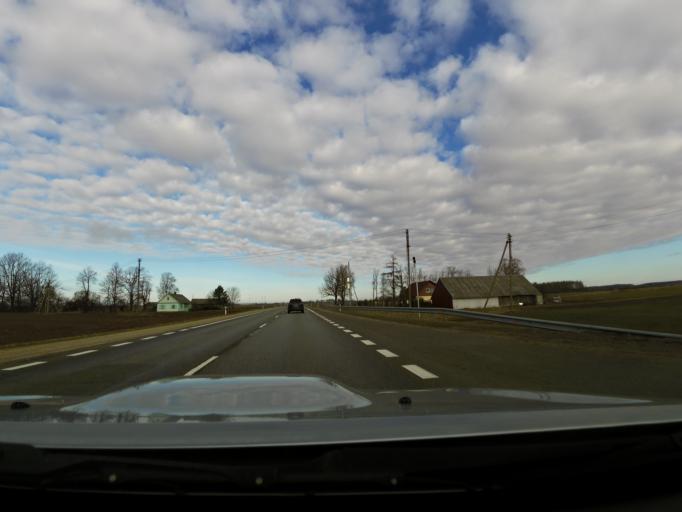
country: LT
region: Siauliu apskritis
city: Pakruojis
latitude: 55.7750
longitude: 24.0551
